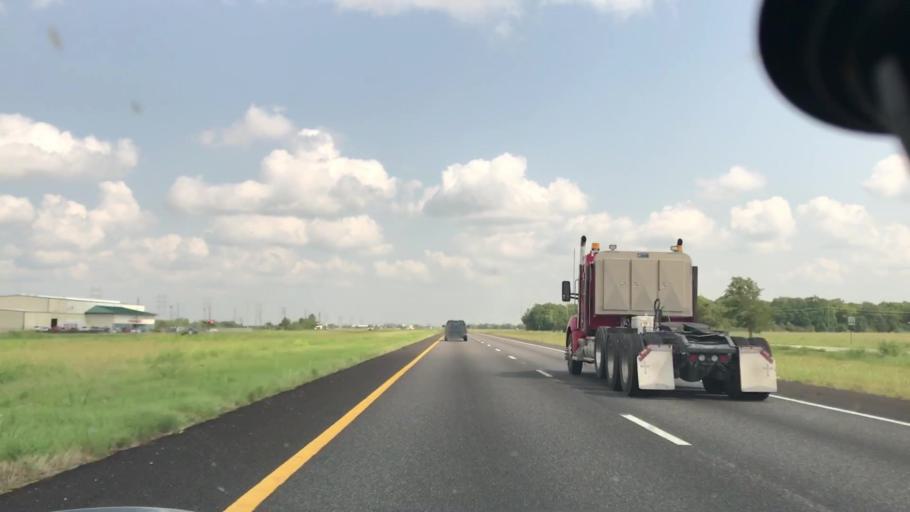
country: US
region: Texas
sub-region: Brazoria County
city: Rosharon
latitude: 29.4015
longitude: -95.4267
